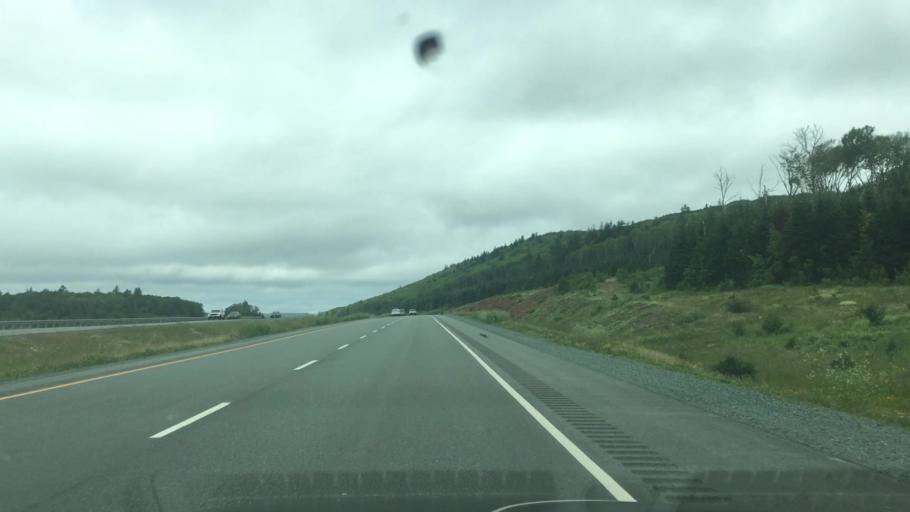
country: CA
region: Nova Scotia
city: Oxford
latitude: 45.5139
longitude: -63.6975
